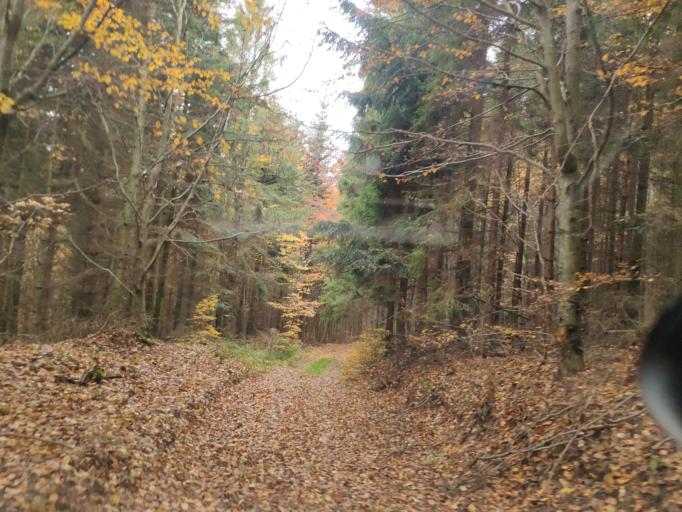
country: SK
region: Kosicky
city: Medzev
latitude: 48.7498
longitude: 20.9835
